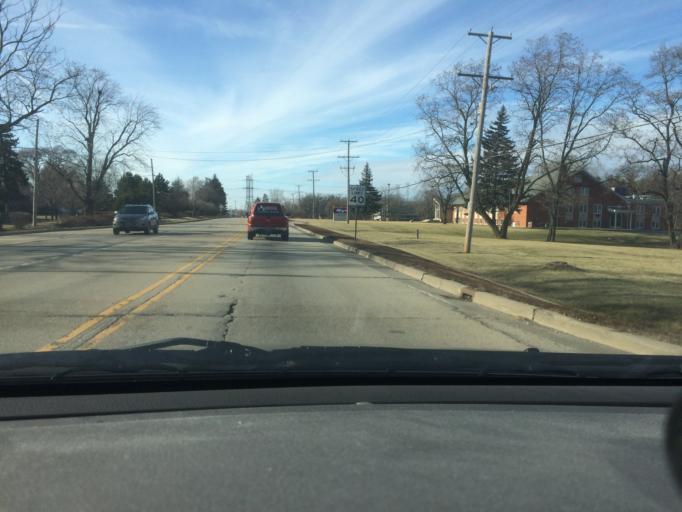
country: US
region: Illinois
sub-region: Cook County
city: Streamwood
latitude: 42.0303
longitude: -88.2298
